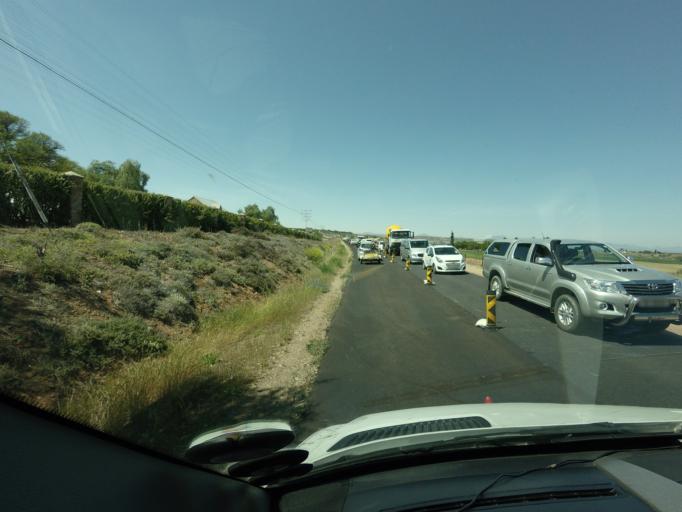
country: ZA
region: Western Cape
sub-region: Eden District Municipality
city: Oudtshoorn
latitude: -33.5186
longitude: 22.2436
